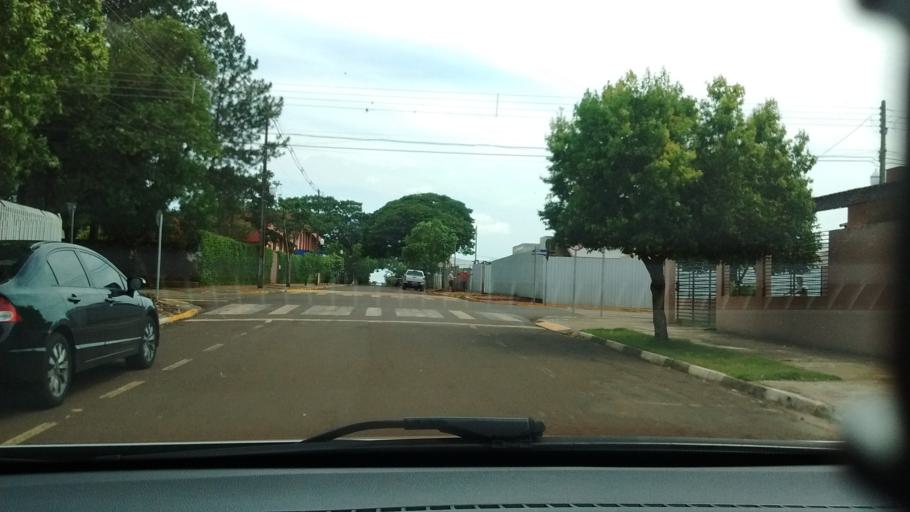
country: BR
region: Parana
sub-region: Corbelia
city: Corbelia
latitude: -24.5438
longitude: -52.9888
